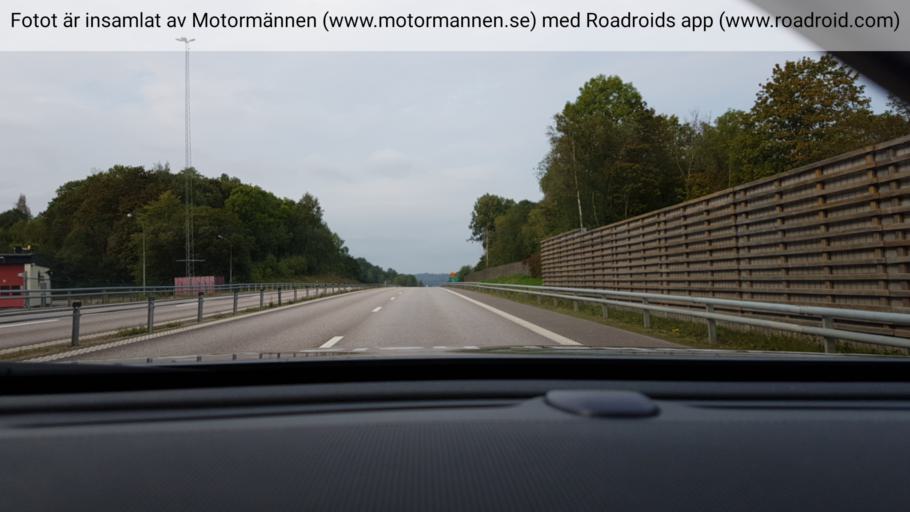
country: SE
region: Vaestra Goetaland
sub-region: Lilla Edets Kommun
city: Lilla Edet
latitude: 58.1310
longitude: 12.1369
